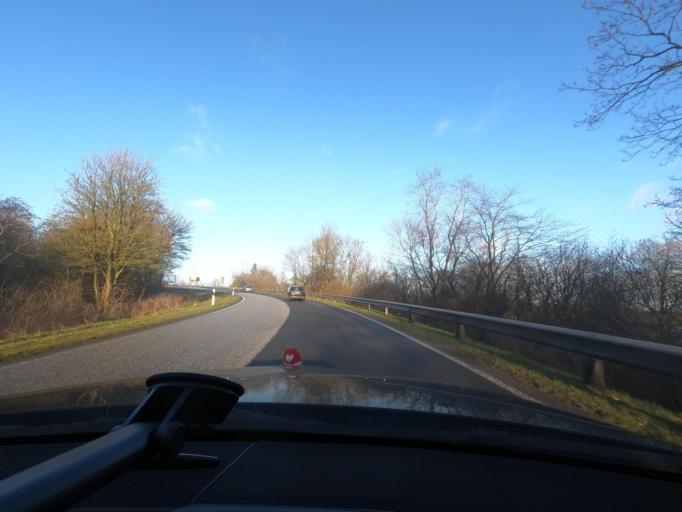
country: DE
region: Schleswig-Holstein
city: Jarplund-Weding
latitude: 54.7331
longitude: 9.3918
